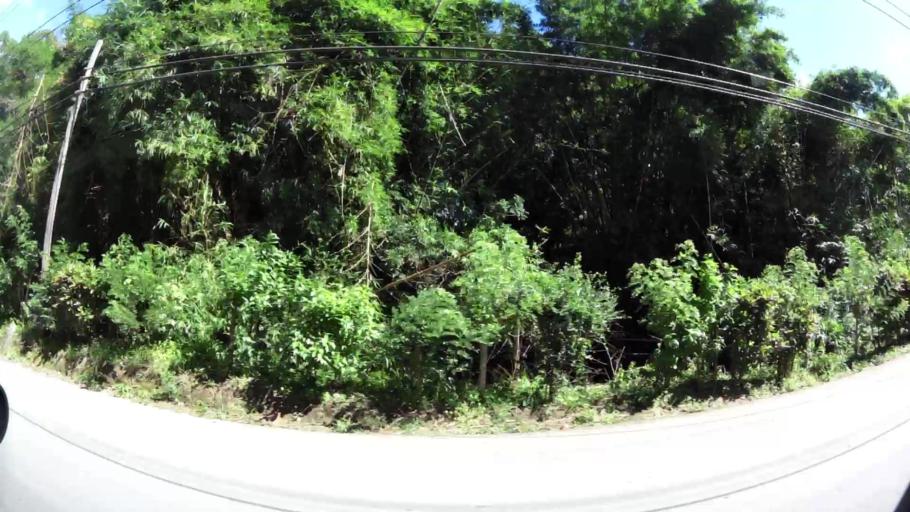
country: TT
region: Tobago
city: Scarborough
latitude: 11.2252
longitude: -60.7631
